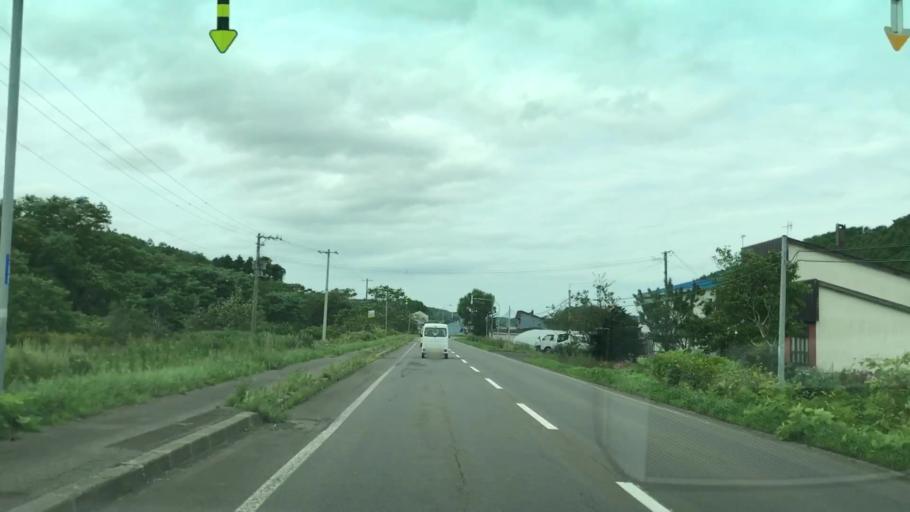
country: JP
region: Hokkaido
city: Iwanai
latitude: 42.9663
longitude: 140.6882
